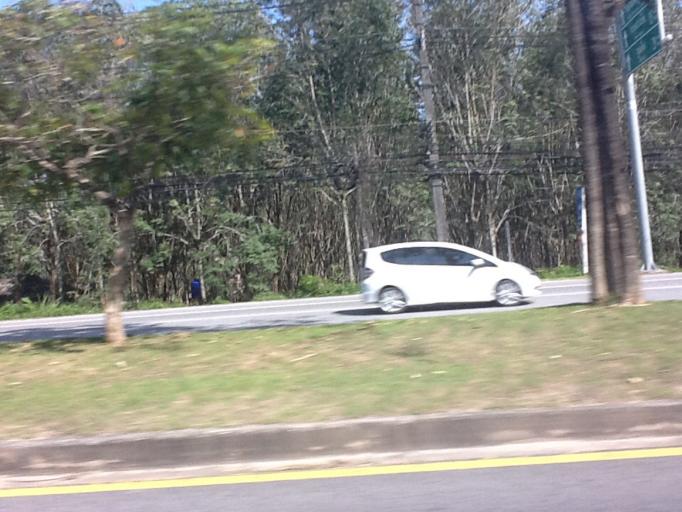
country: TH
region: Phuket
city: Thalang
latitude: 8.1177
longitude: 98.3360
